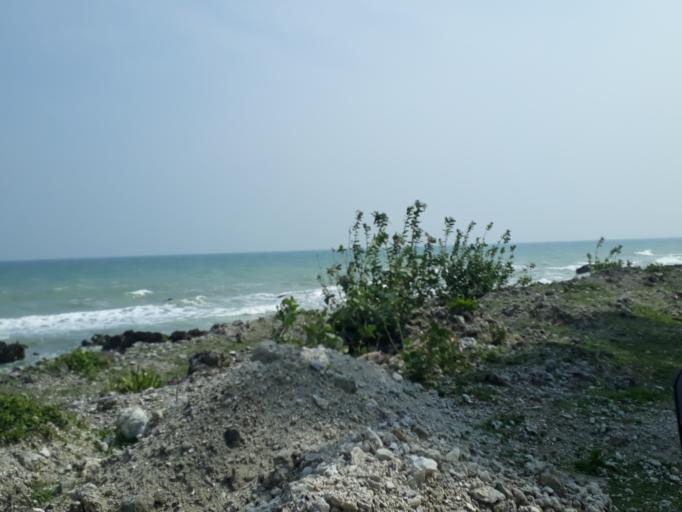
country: LK
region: Northern Province
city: Jaffna
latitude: 9.5288
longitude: 79.7188
